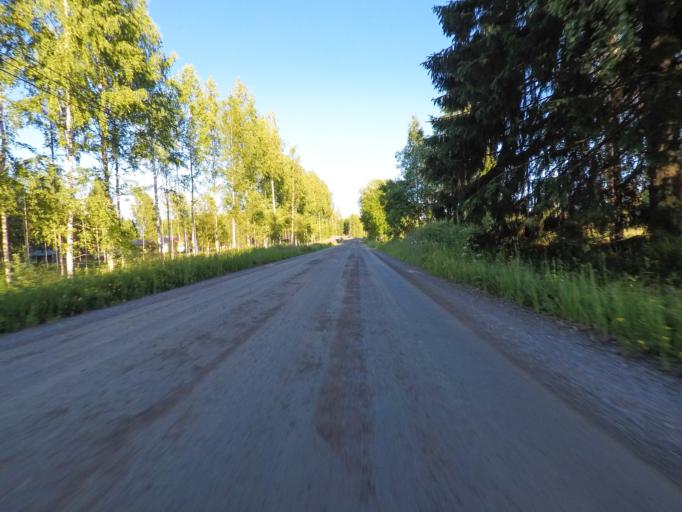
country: FI
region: Northern Savo
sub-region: Kuopio
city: Maaninka
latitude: 62.8777
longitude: 27.2990
